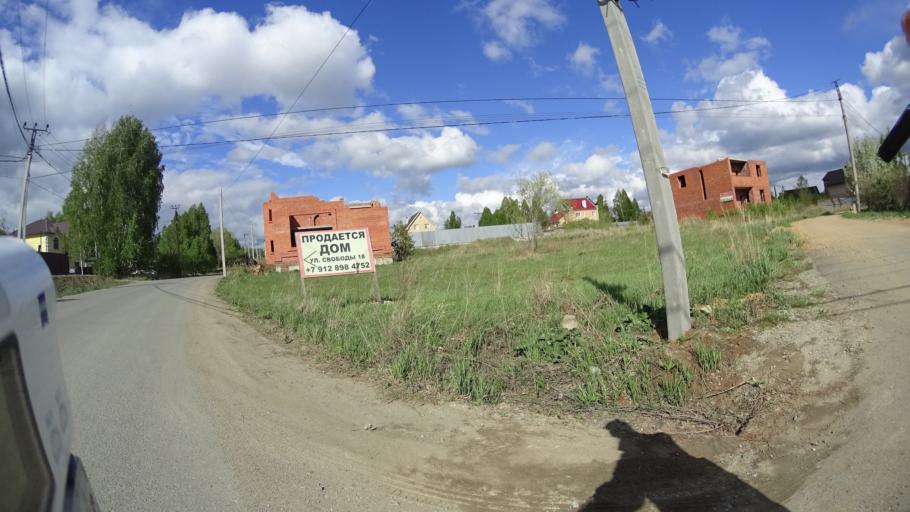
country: RU
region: Chelyabinsk
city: Sargazy
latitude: 55.1573
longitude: 61.2416
